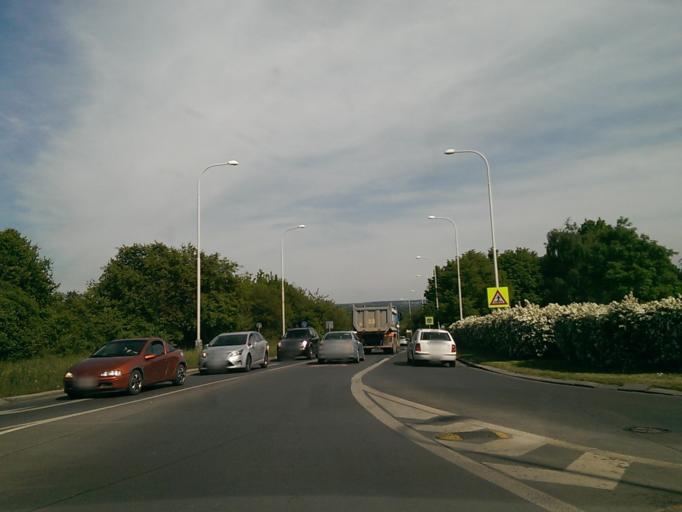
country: CZ
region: Central Bohemia
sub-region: Okres Praha-Zapad
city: Pruhonice
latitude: 50.0339
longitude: 14.5377
